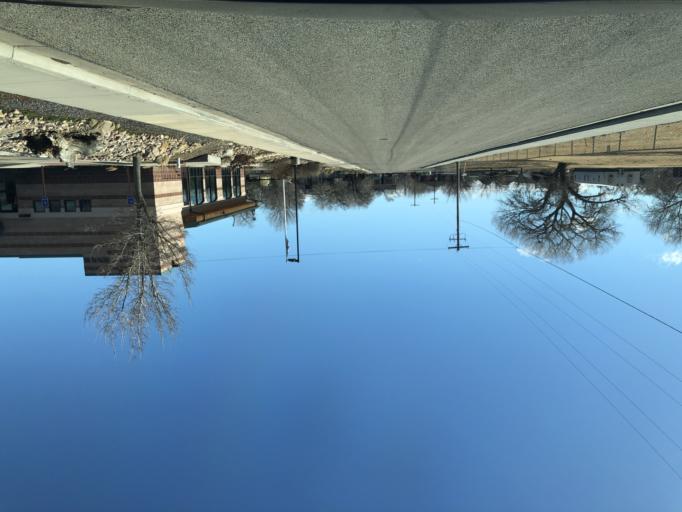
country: US
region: Utah
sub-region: Carbon County
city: East Carbon City
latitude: 38.9933
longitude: -110.1576
